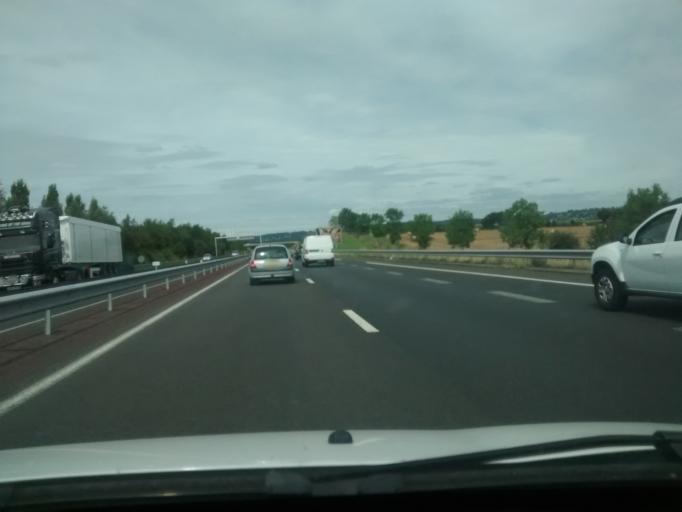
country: FR
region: Lower Normandy
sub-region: Departement de la Manche
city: Saint-Quentin-sur-le-Homme
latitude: 48.6251
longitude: -1.3378
